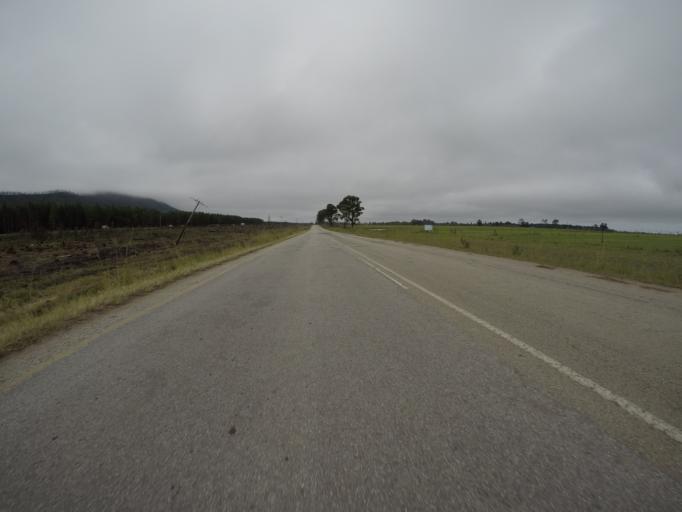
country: ZA
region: Eastern Cape
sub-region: Cacadu District Municipality
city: Kareedouw
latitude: -33.9829
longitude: 24.0555
